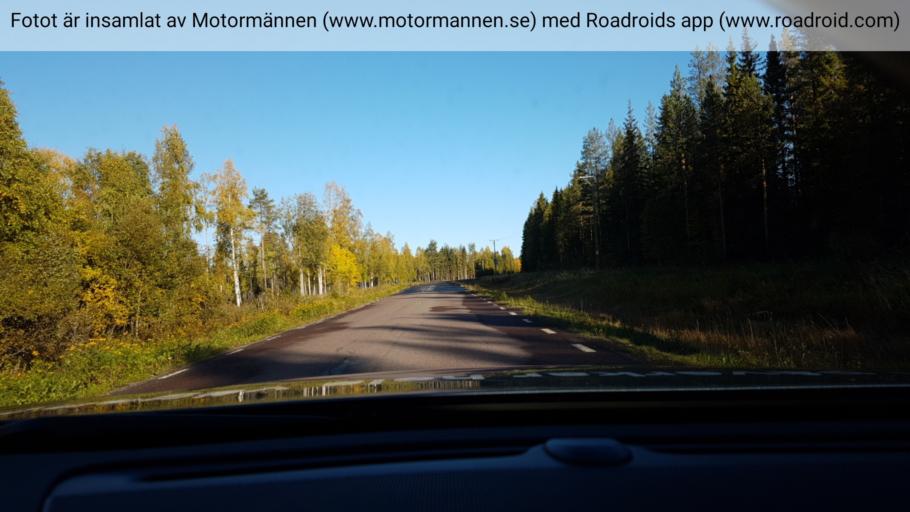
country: SE
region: Norrbotten
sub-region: Bodens Kommun
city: Boden
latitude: 66.0803
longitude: 21.3867
